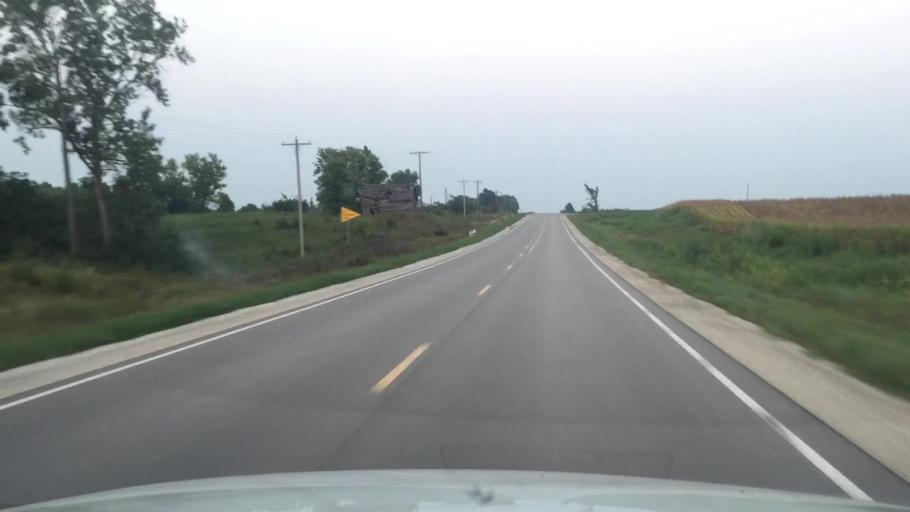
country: US
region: Iowa
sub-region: Warren County
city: Indianola
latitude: 41.1826
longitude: -93.4834
